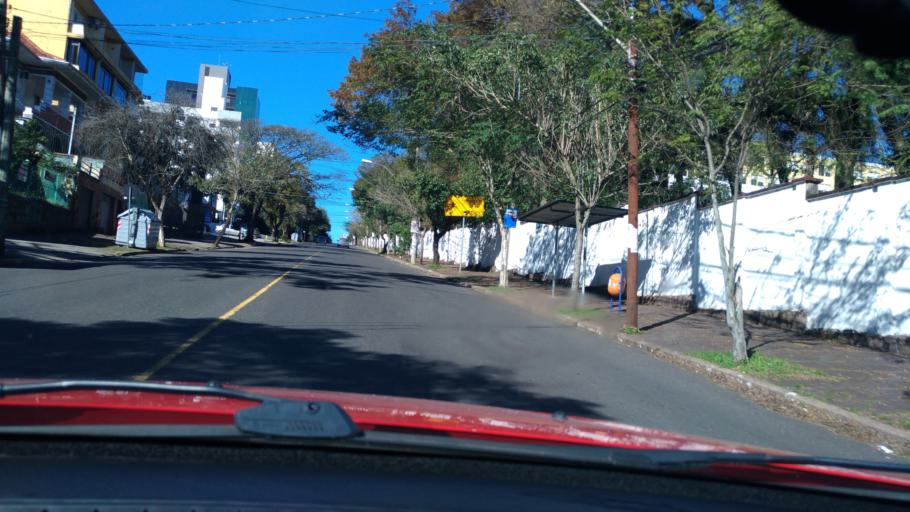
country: BR
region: Rio Grande do Sul
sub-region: Porto Alegre
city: Porto Alegre
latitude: -30.0178
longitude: -51.1940
